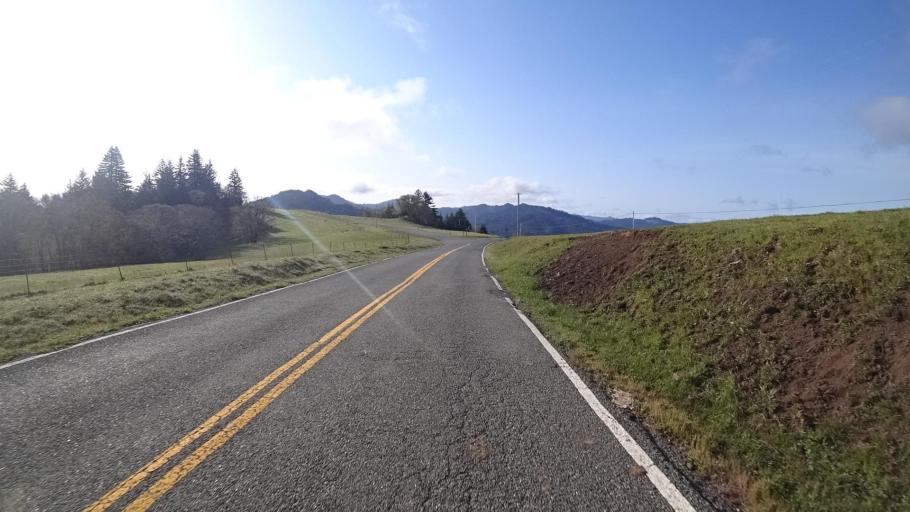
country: US
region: California
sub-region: Humboldt County
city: Blue Lake
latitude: 40.7214
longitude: -123.9430
